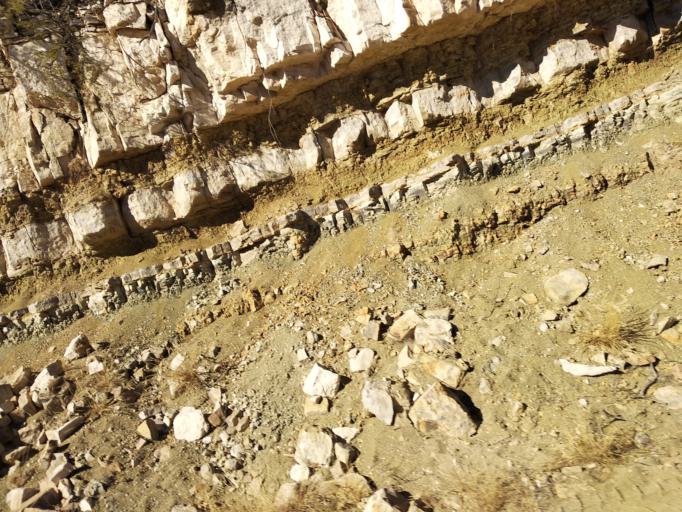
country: BO
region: Cochabamba
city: Mizque
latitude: -18.0856
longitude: -65.7521
